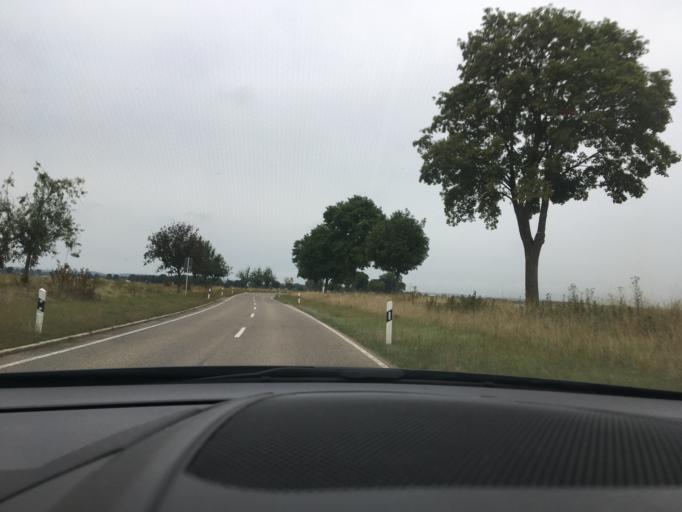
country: DE
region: Baden-Wuerttemberg
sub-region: Tuebingen Region
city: Kirchdorf
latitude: 48.0791
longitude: 10.1072
